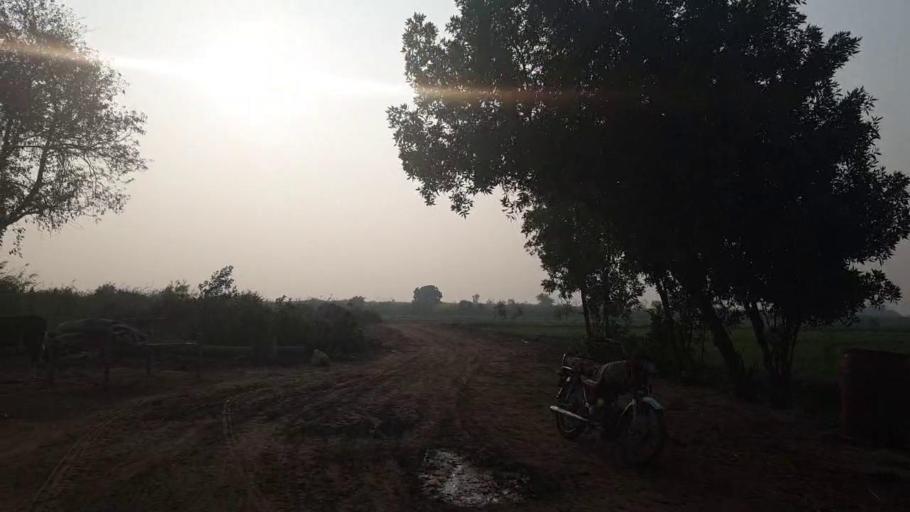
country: PK
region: Sindh
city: Hyderabad
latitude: 25.3218
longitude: 68.4735
